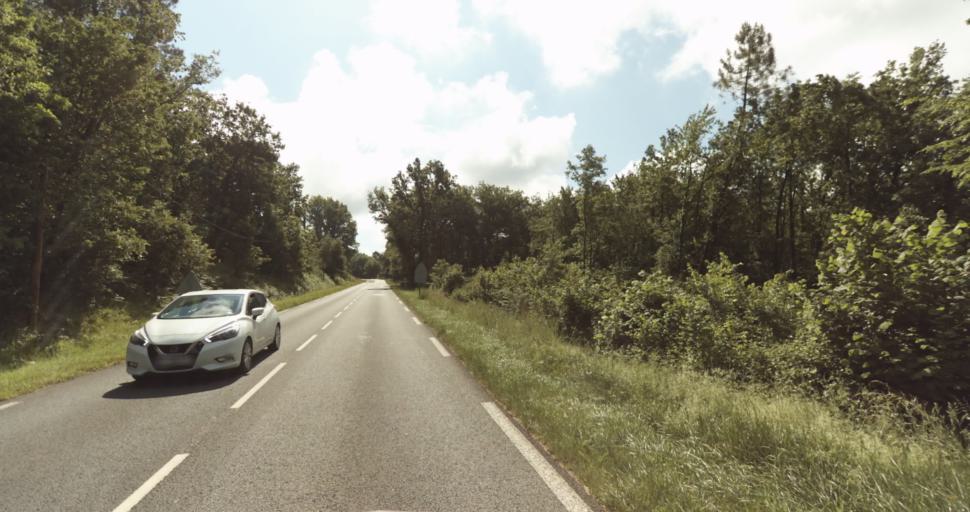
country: FR
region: Aquitaine
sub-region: Departement de la Dordogne
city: Le Bugue
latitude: 44.8395
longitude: 0.8655
